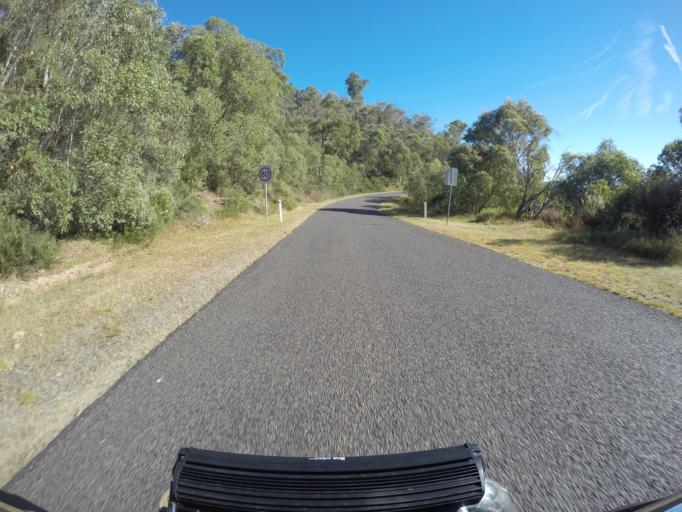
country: AU
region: New South Wales
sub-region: Snowy River
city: Jindabyne
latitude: -36.0549
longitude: 148.2724
